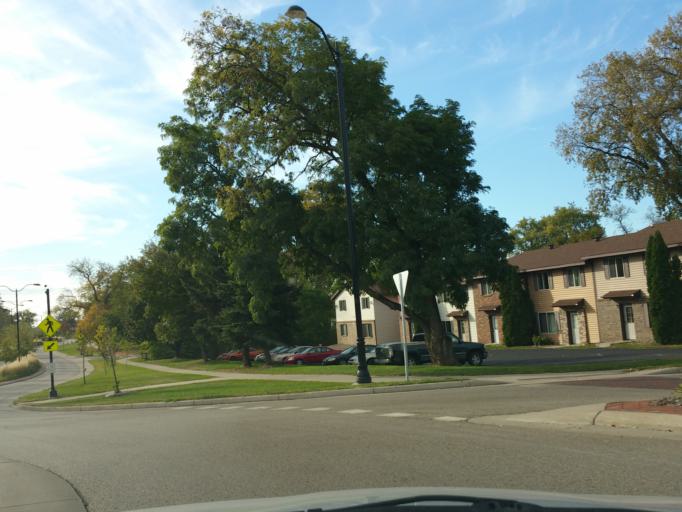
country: US
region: Wisconsin
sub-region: Pierce County
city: River Falls
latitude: 44.8542
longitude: -92.6191
